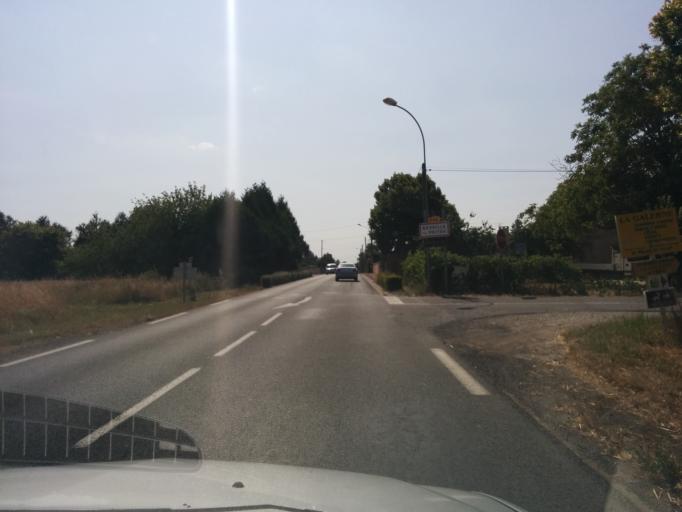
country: FR
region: Poitou-Charentes
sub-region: Departement de la Vienne
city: Neuville-de-Poitou
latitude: 46.6875
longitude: 0.2770
